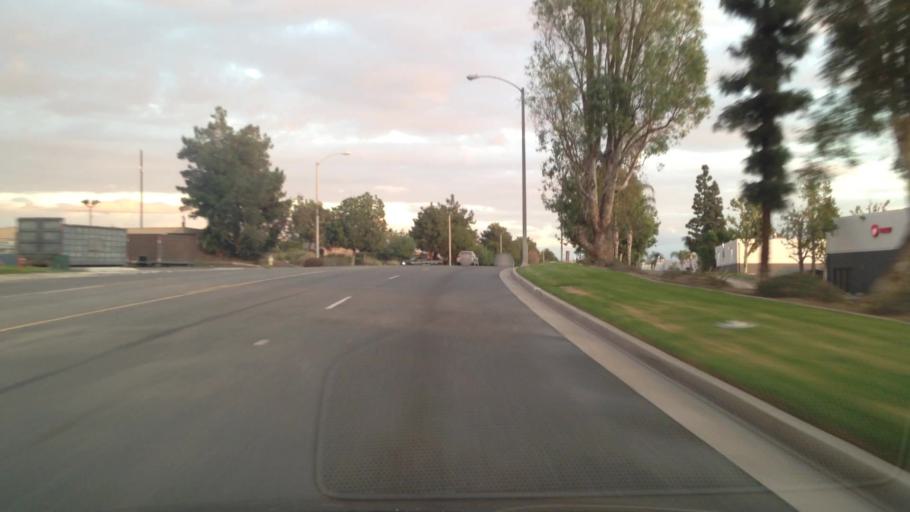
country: US
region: California
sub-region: Riverside County
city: Pedley
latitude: 33.9561
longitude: -117.4455
